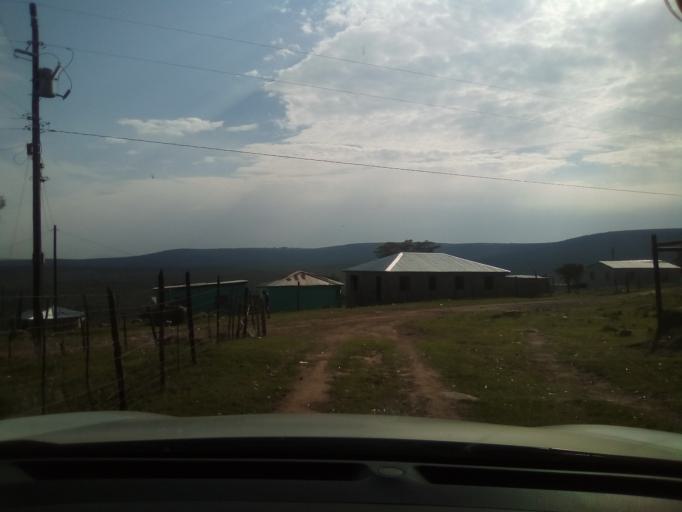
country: ZA
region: Eastern Cape
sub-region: Buffalo City Metropolitan Municipality
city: Bhisho
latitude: -32.9848
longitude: 27.2586
